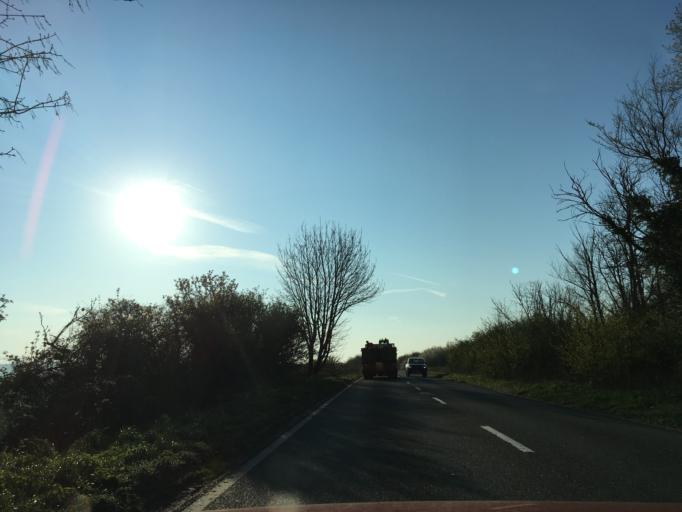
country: GB
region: England
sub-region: Oxfordshire
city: Burford
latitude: 51.8093
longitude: -1.6676
